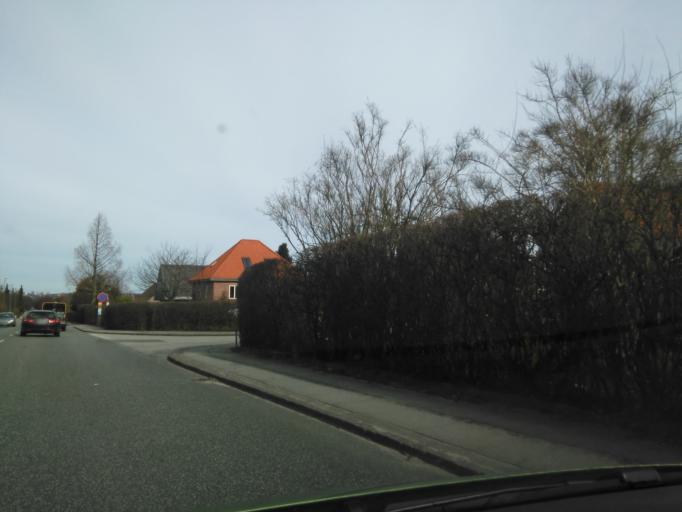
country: DK
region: Central Jutland
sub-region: Arhus Kommune
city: Arhus
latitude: 56.1237
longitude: 10.1861
